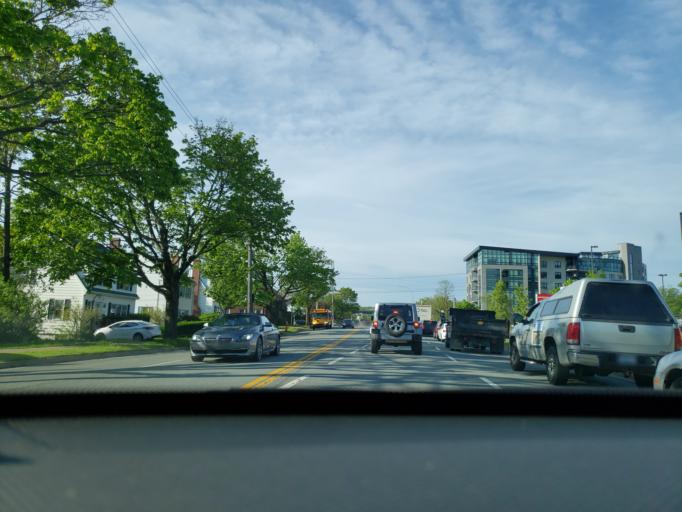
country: CA
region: Nova Scotia
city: Dartmouth
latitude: 44.6548
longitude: -63.6300
